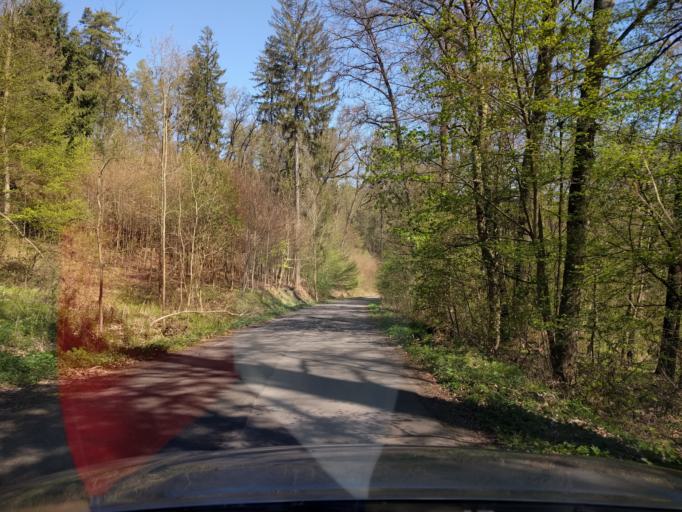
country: CZ
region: Central Bohemia
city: Kostelec nad Cernymi Lesy
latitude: 50.0334
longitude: 14.8282
